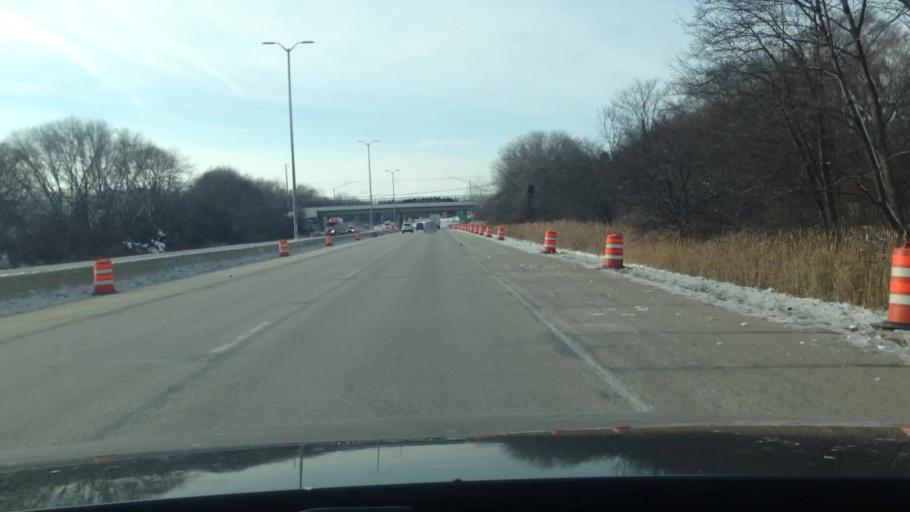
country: US
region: Wisconsin
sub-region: Milwaukee County
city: Hales Corners
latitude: 42.9577
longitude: -88.0658
